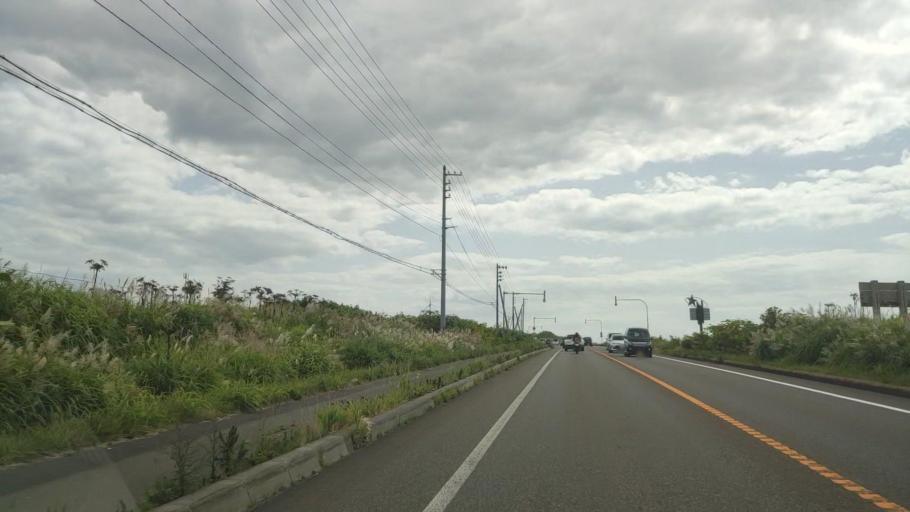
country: JP
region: Hokkaido
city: Rumoi
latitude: 44.5268
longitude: 141.7656
